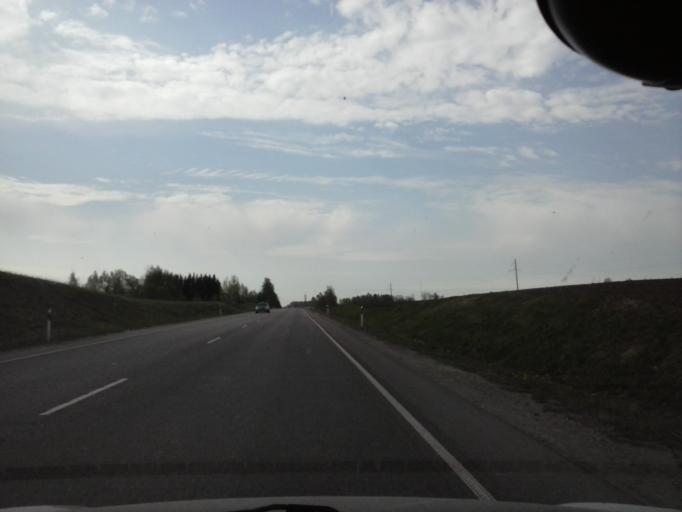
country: EE
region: Tartu
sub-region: UElenurme vald
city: Ulenurme
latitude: 58.1632
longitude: 26.6924
